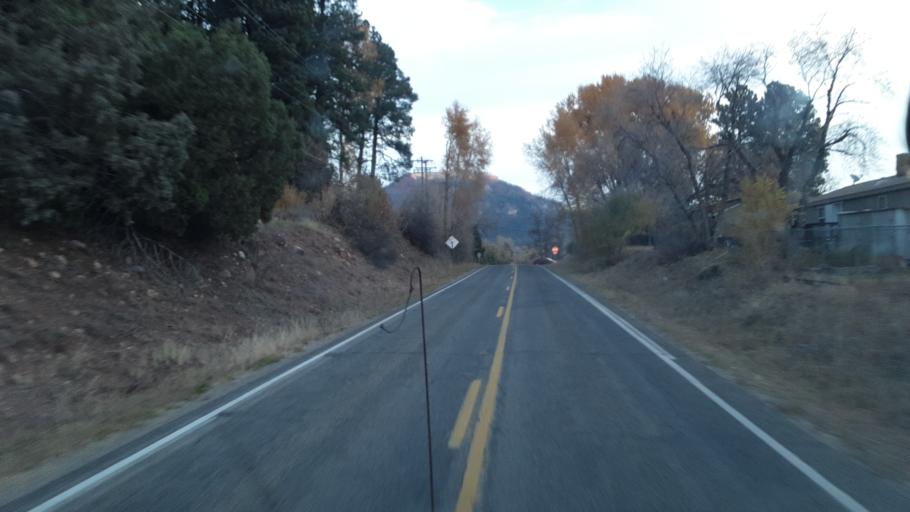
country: US
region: Colorado
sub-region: La Plata County
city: Durango
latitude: 37.3889
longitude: -107.8493
